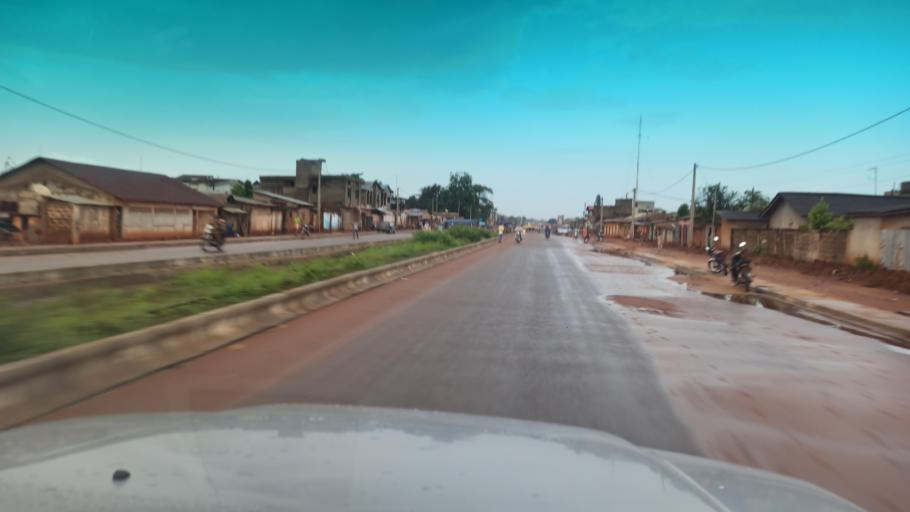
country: BJ
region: Queme
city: Porto-Novo
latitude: 6.4989
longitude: 2.6264
